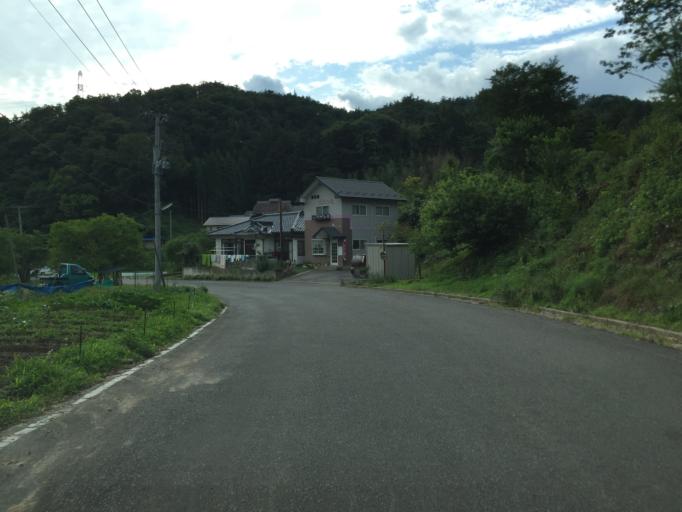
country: JP
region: Fukushima
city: Fukushima-shi
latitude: 37.7012
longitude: 140.5205
